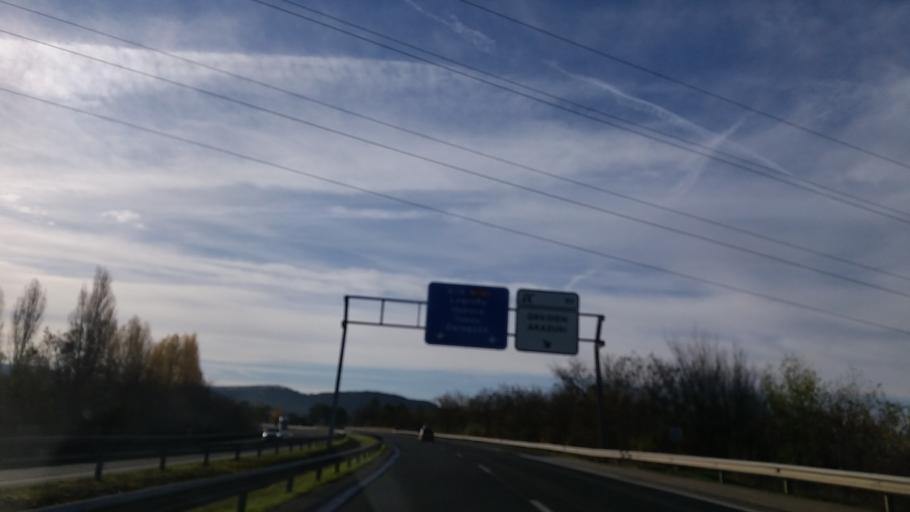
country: ES
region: Navarre
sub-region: Provincia de Navarra
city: Orkoien
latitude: 42.8205
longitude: -1.7146
